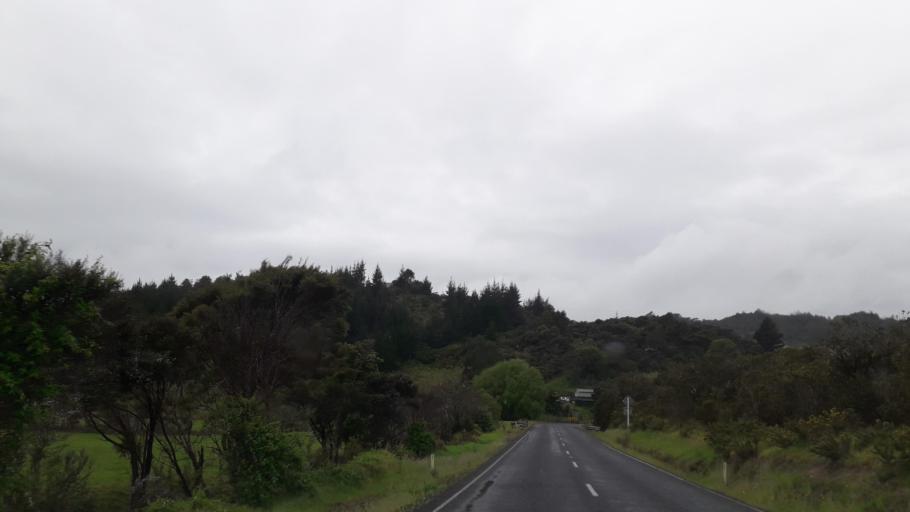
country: NZ
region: Northland
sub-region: Far North District
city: Kaitaia
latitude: -35.3732
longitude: 173.5071
